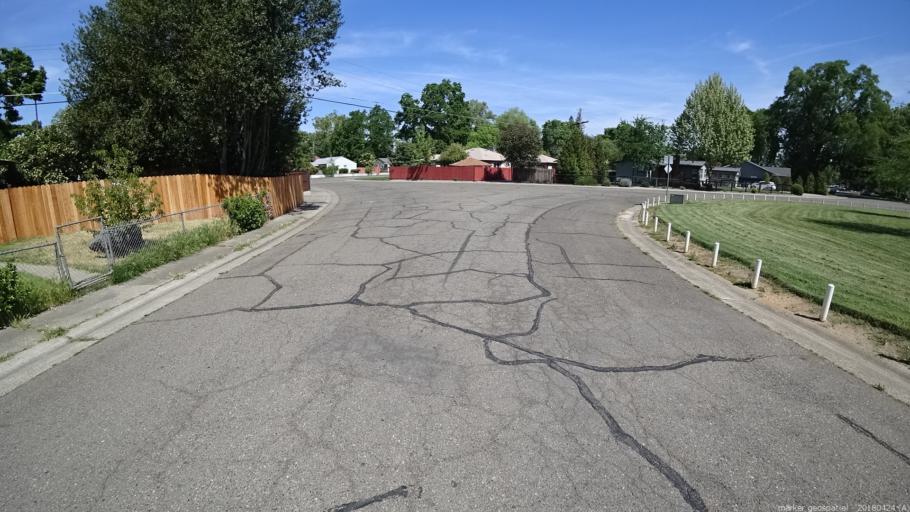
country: US
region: California
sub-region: Yolo County
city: West Sacramento
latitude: 38.5667
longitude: -121.5308
